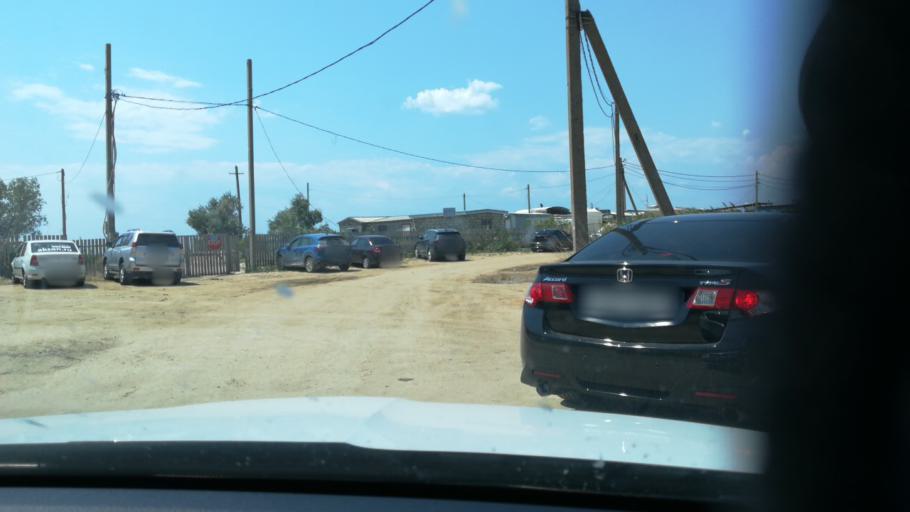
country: RU
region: Krasnodarskiy
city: Vyshestebliyevskaya
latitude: 45.1123
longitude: 36.8727
